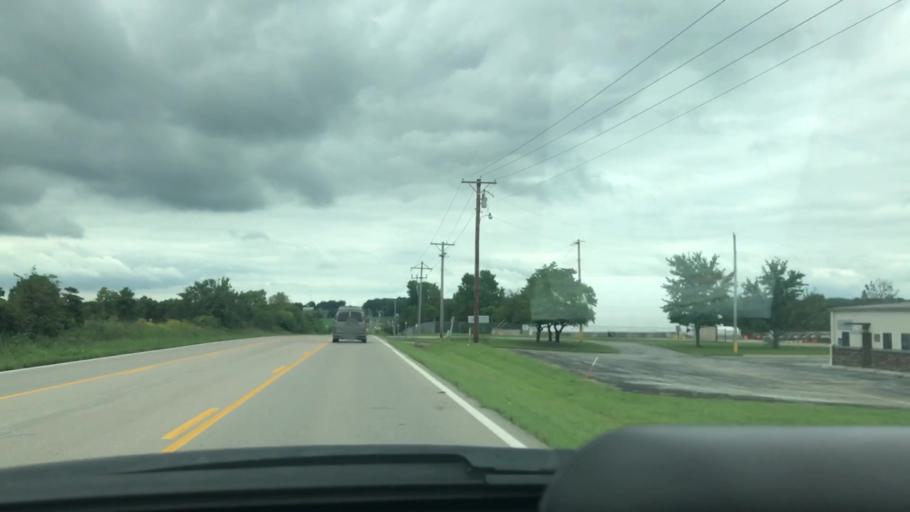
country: US
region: Missouri
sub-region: Dallas County
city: Buffalo
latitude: 37.6596
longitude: -93.1036
